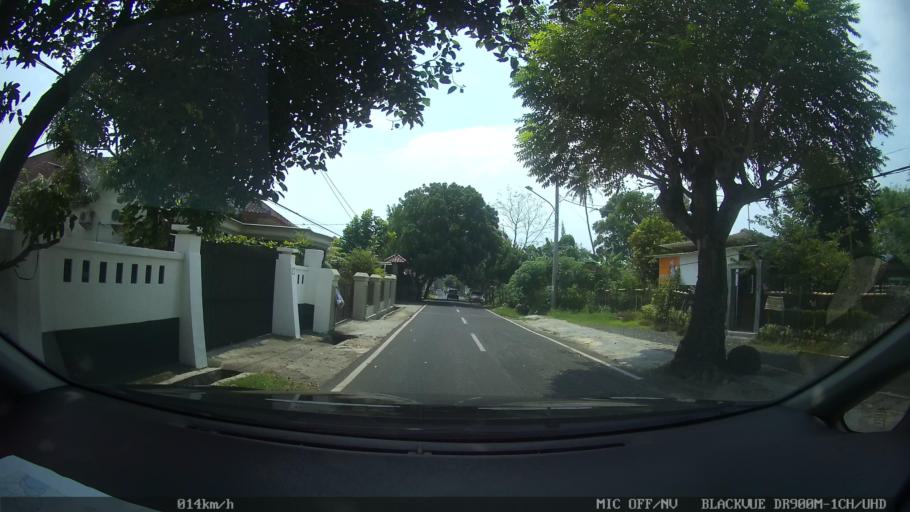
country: ID
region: Lampung
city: Bandarlampung
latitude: -5.4257
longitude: 105.2629
